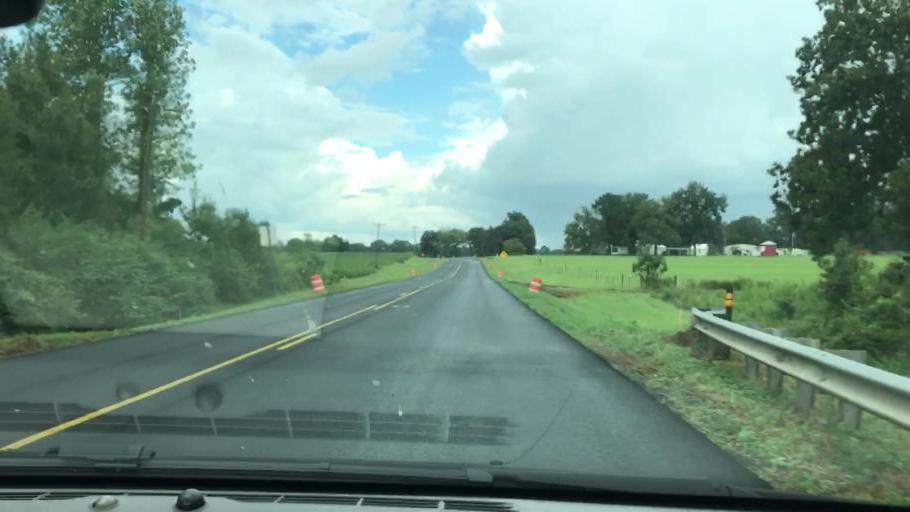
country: US
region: Georgia
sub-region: Early County
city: Blakely
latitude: 31.4255
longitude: -84.9668
